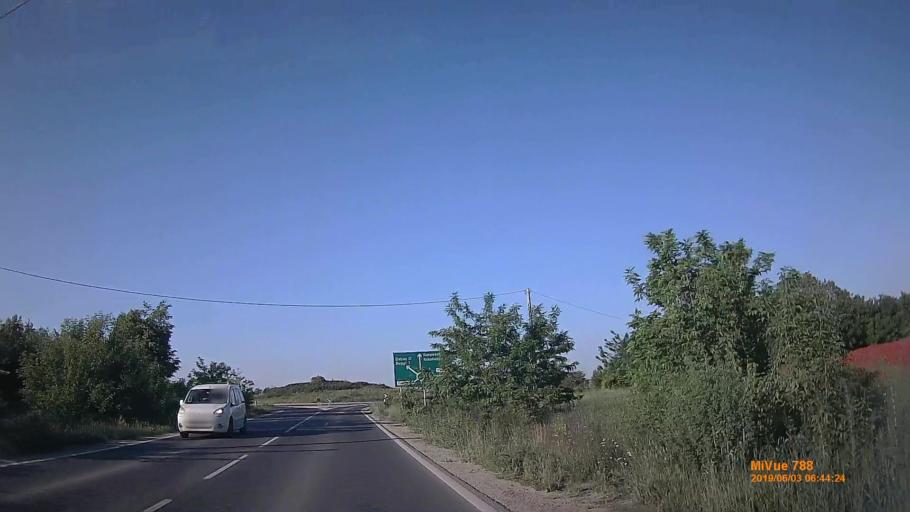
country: HU
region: Pest
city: Bugyi
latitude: 47.2444
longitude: 19.1290
